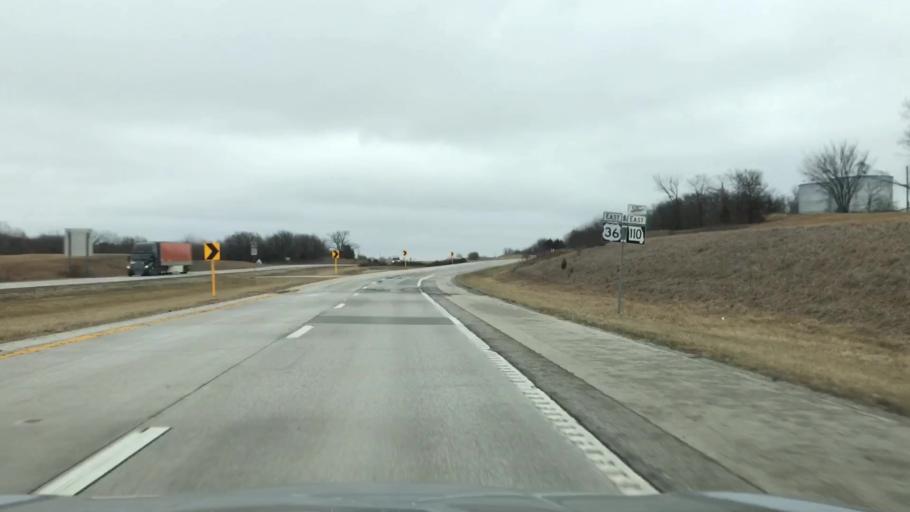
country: US
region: Missouri
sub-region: Linn County
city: Marceline
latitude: 39.7609
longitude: -92.9322
